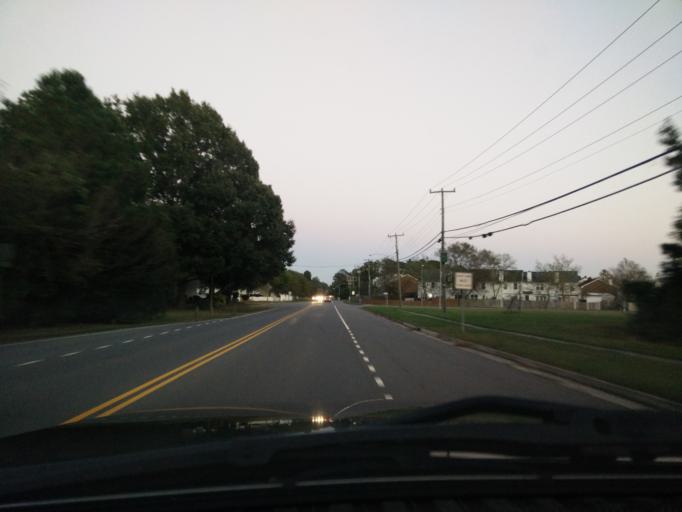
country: US
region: Virginia
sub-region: City of Chesapeake
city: Chesapeake
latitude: 36.7521
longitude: -76.2432
